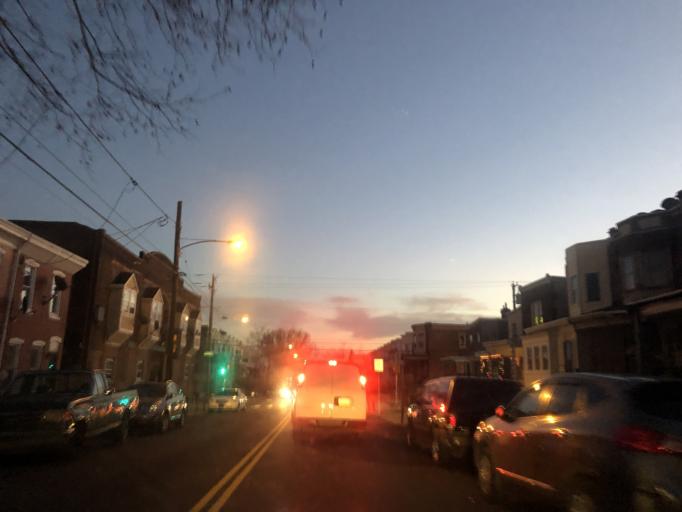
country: US
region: Pennsylvania
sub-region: Delaware County
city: Millbourne
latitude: 39.9751
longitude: -75.2385
